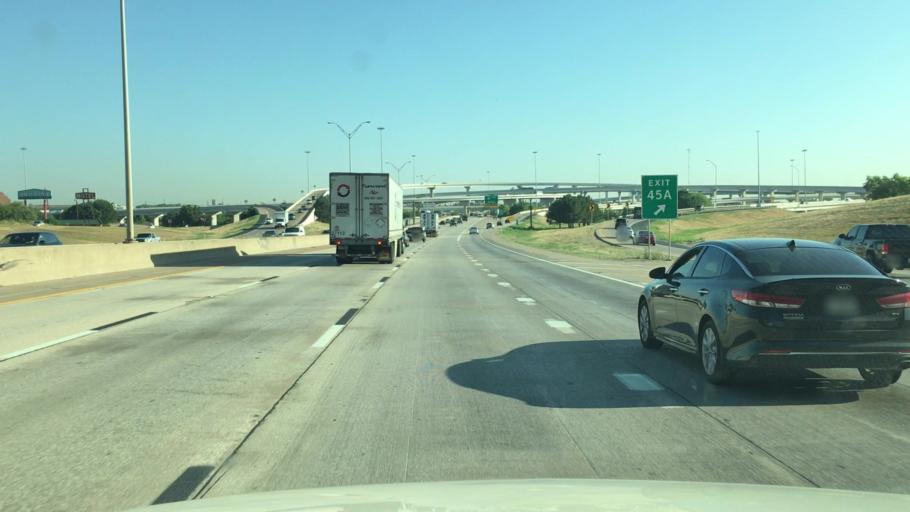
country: US
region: Texas
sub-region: Tarrant County
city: Edgecliff Village
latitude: 32.6606
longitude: -97.3211
